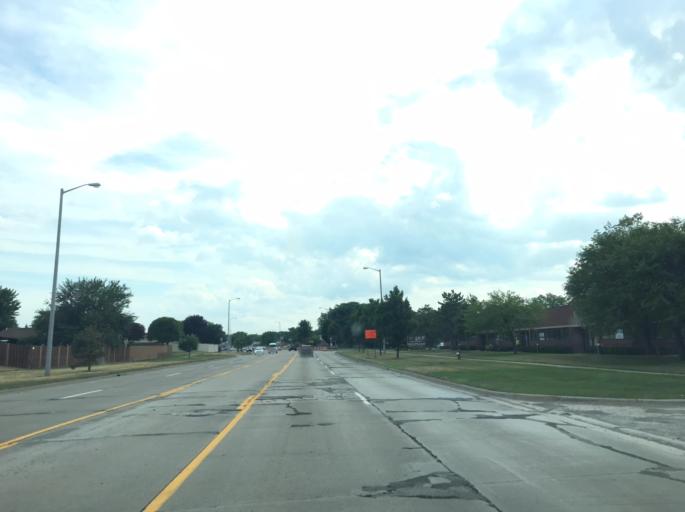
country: US
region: Michigan
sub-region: Macomb County
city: Fraser
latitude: 42.5559
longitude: -82.9885
